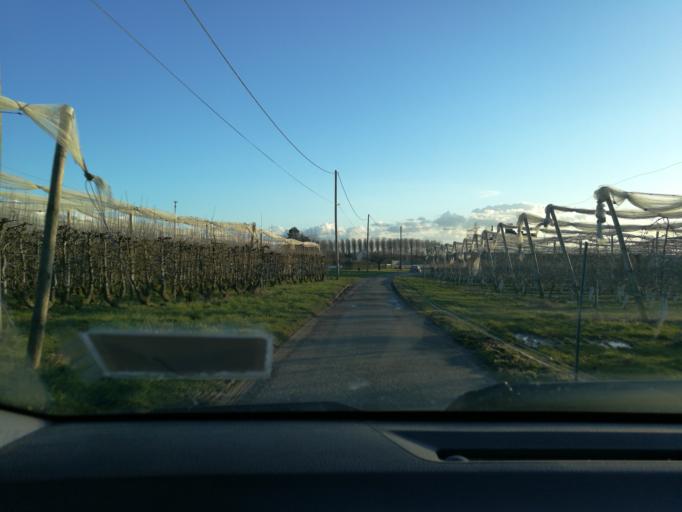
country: FR
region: Centre
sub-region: Departement du Loiret
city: Semoy
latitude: 47.9402
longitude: 1.9649
